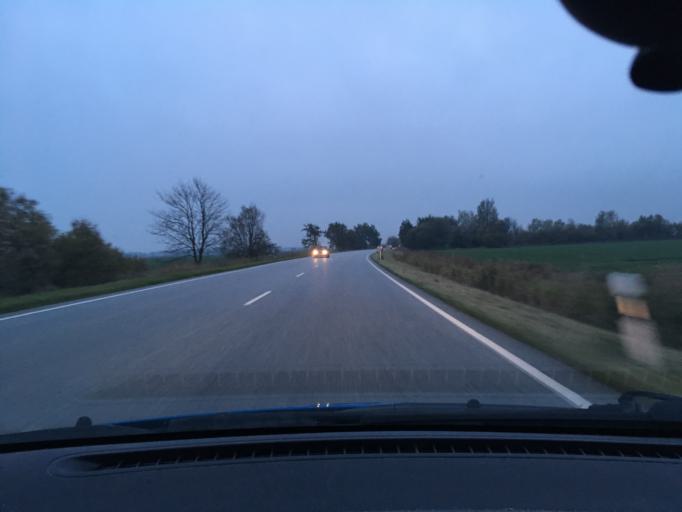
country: DE
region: Schleswig-Holstein
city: Lohe-Rickelshof
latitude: 54.2107
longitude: 9.0475
